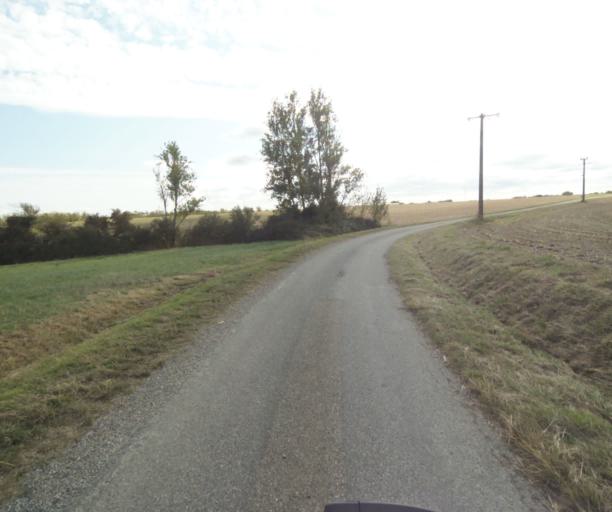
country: FR
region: Midi-Pyrenees
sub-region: Departement du Tarn-et-Garonne
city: Finhan
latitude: 43.8762
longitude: 1.1874
